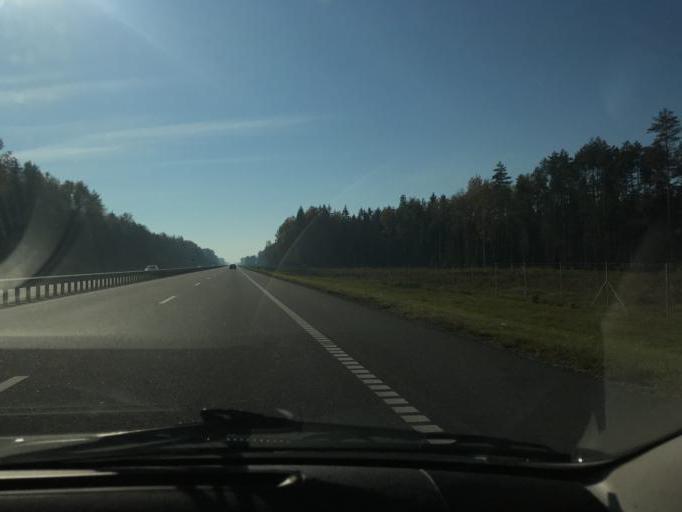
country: BY
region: Minsk
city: Slutsk
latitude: 53.2644
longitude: 27.5501
